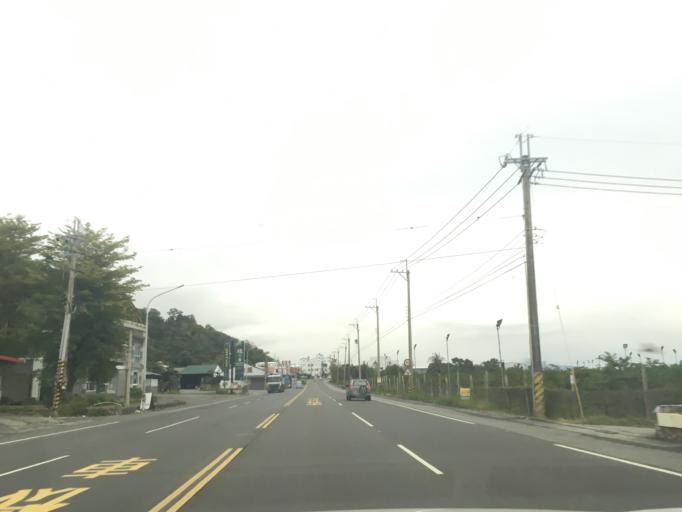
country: TW
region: Taiwan
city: Taitung City
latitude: 22.6812
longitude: 121.0424
